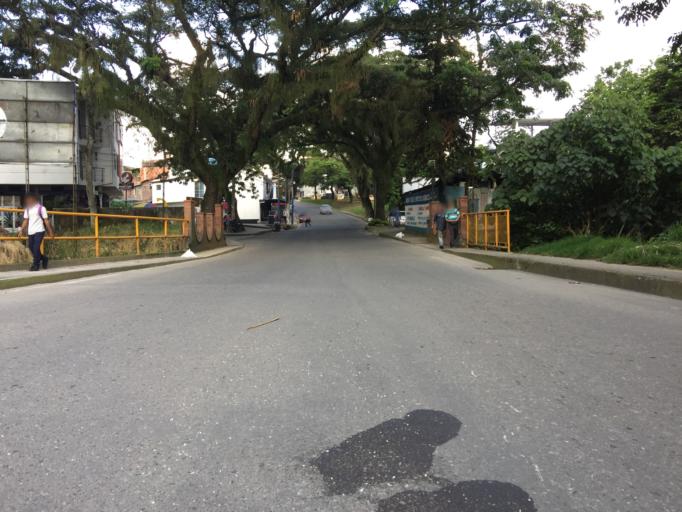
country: CO
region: Tolima
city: Ibague
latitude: 4.4476
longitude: -75.2036
